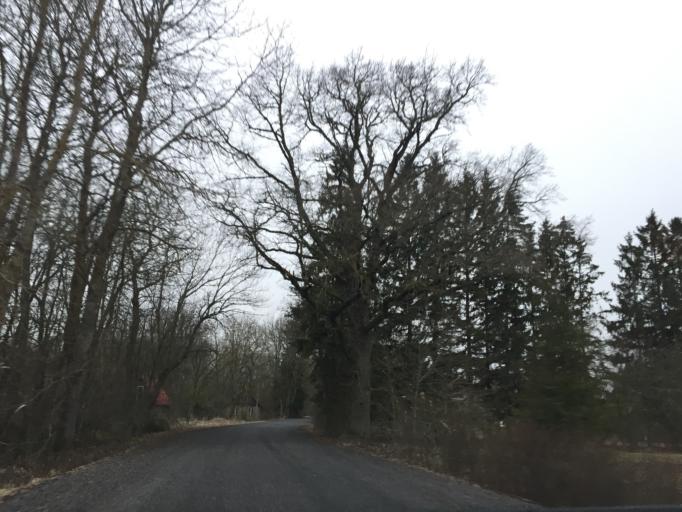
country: EE
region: Laeaene
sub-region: Lihula vald
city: Lihula
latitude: 58.6544
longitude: 23.6059
